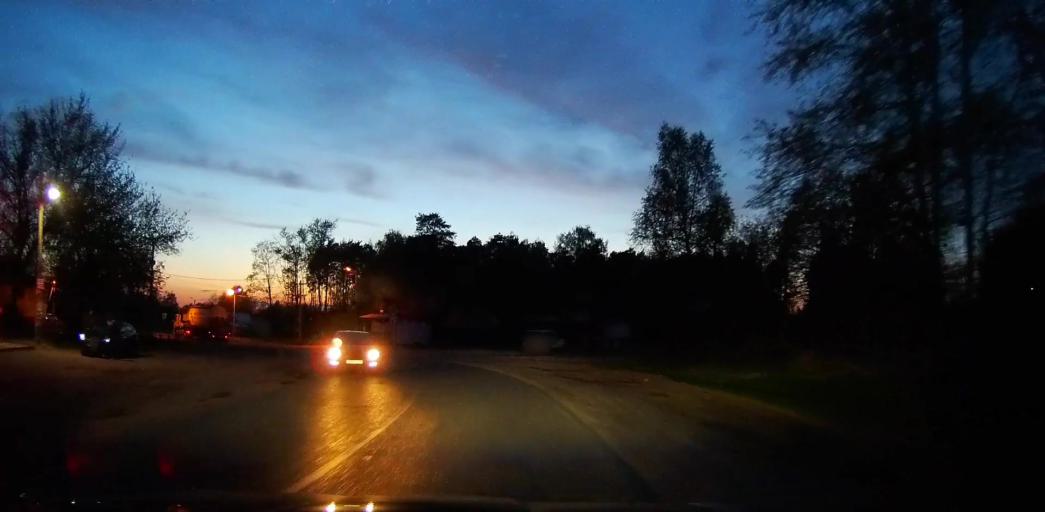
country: RU
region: Moskovskaya
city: Peski
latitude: 55.2158
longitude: 38.7703
